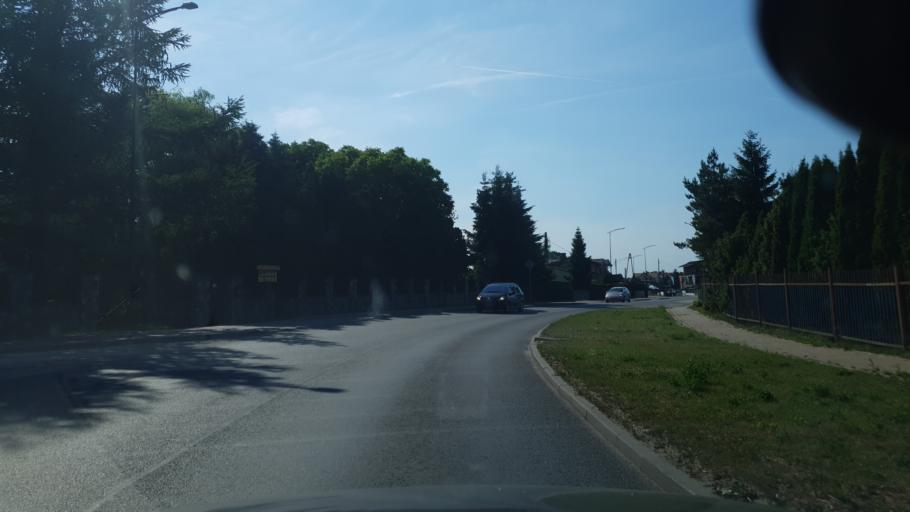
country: PL
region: Pomeranian Voivodeship
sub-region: Powiat kartuski
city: Chwaszczyno
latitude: 54.4427
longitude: 18.4241
